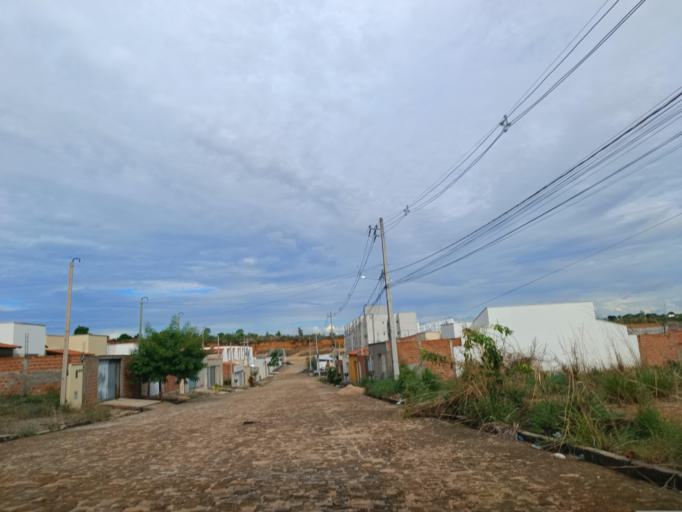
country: BR
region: Piaui
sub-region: Teresina
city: Teresina
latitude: -5.1634
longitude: -42.7774
